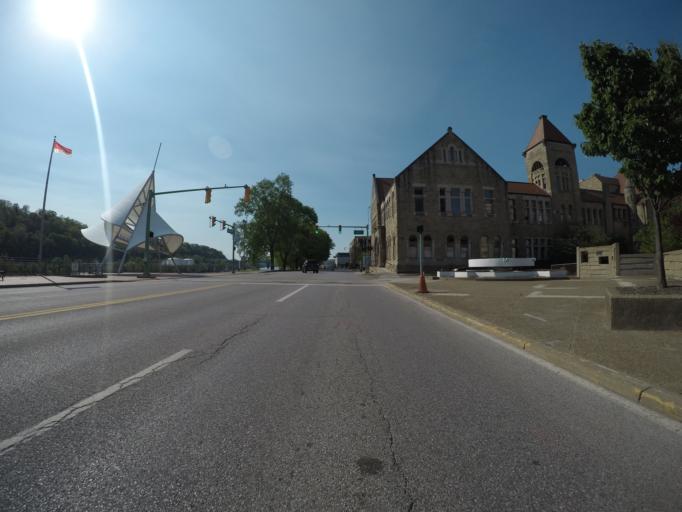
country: US
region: West Virginia
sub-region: Kanawha County
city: Charleston
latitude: 38.3503
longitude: -81.6390
